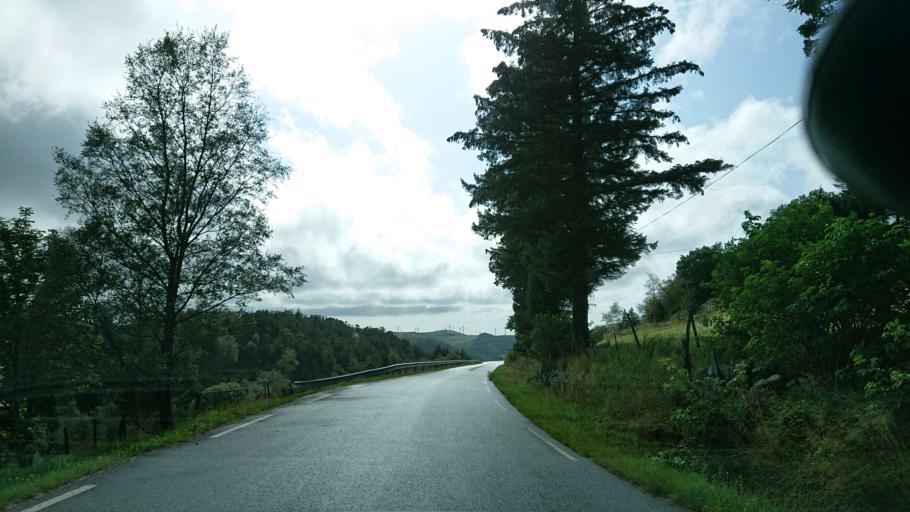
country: NO
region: Rogaland
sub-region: Gjesdal
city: Algard
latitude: 58.6819
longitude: 5.8588
